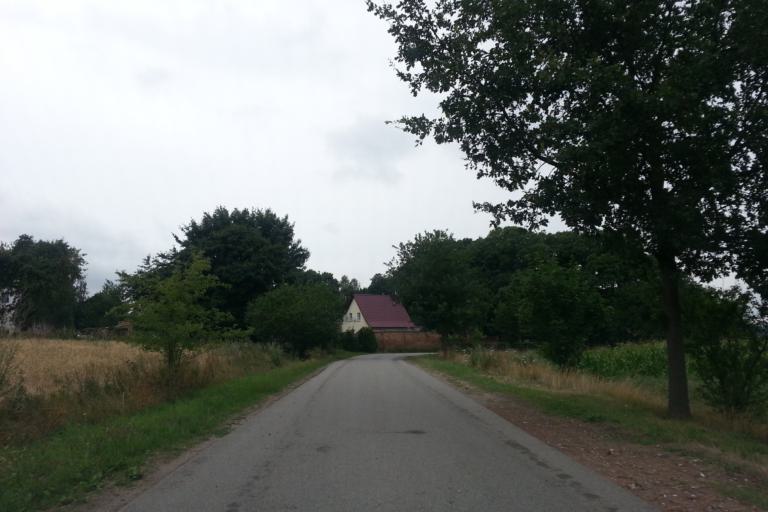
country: DE
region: Mecklenburg-Vorpommern
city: Ferdinandshof
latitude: 53.6748
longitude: 13.9152
